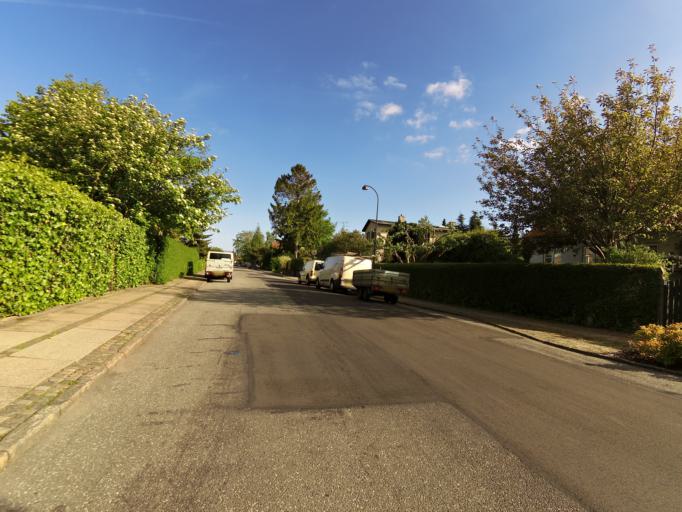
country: DK
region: Capital Region
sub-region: Lyngby-Tarbaek Kommune
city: Kongens Lyngby
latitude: 55.7372
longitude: 12.5321
